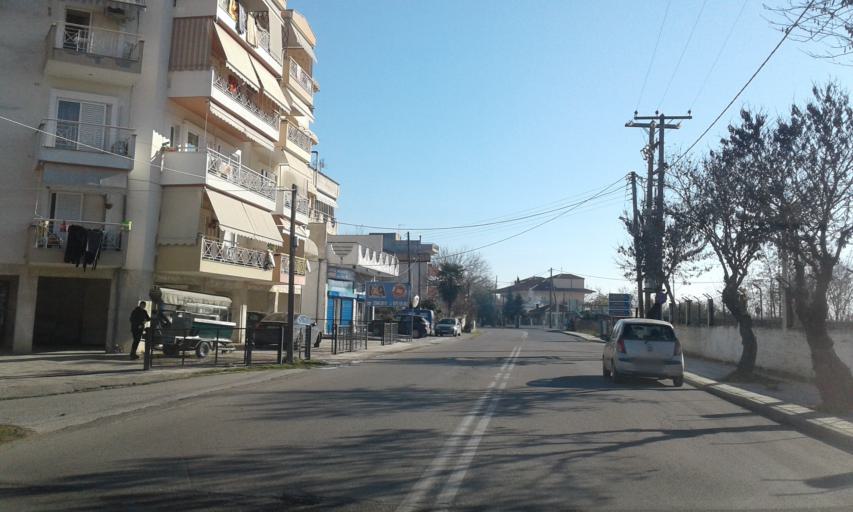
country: GR
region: Central Macedonia
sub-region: Nomos Thessalonikis
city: Lagkadas
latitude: 40.7469
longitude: 23.0636
